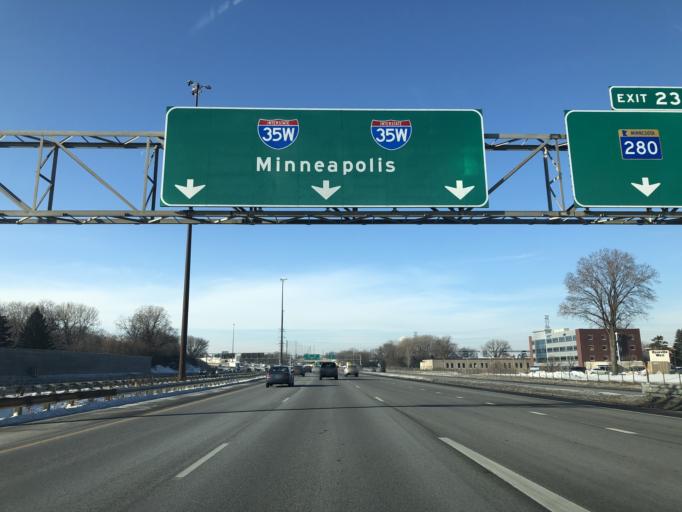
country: US
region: Minnesota
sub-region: Ramsey County
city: Lauderdale
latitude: 45.0118
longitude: -93.1967
